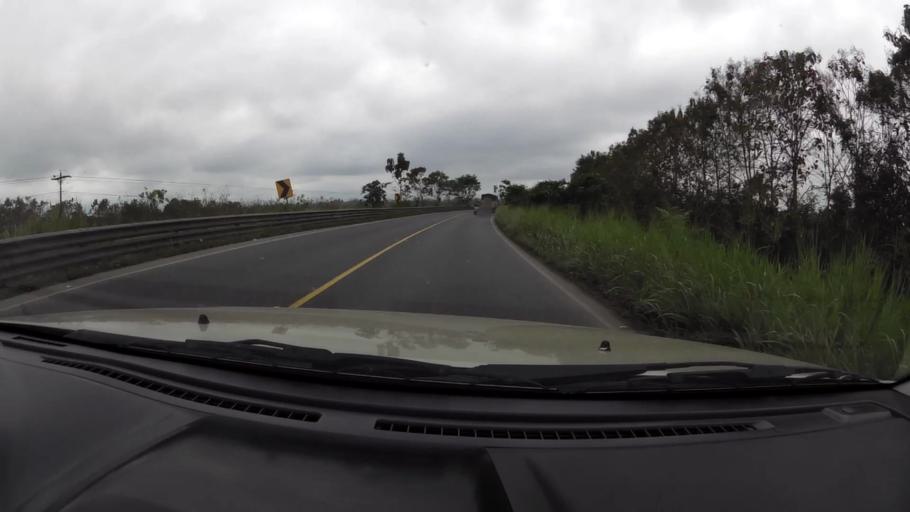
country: EC
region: Guayas
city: Balao
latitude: -2.8176
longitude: -79.7076
